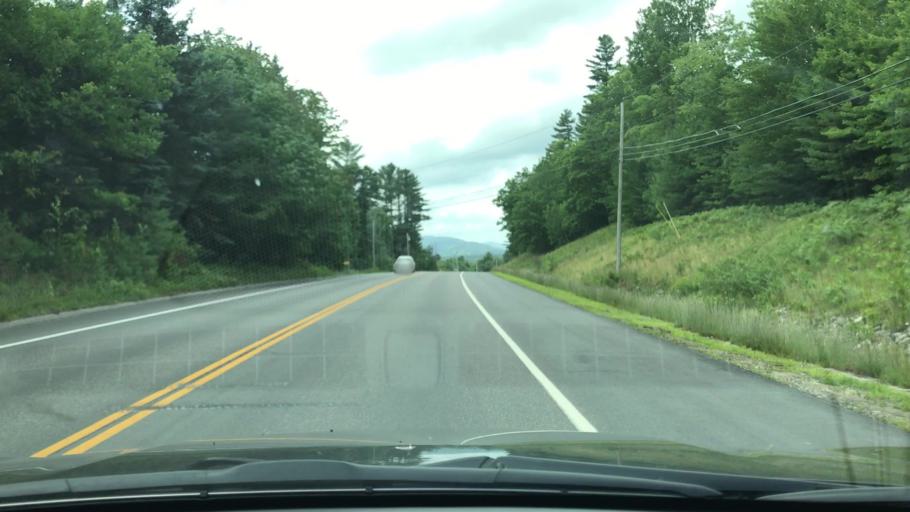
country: US
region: Maine
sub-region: Oxford County
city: Bethel
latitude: 44.4069
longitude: -70.7210
